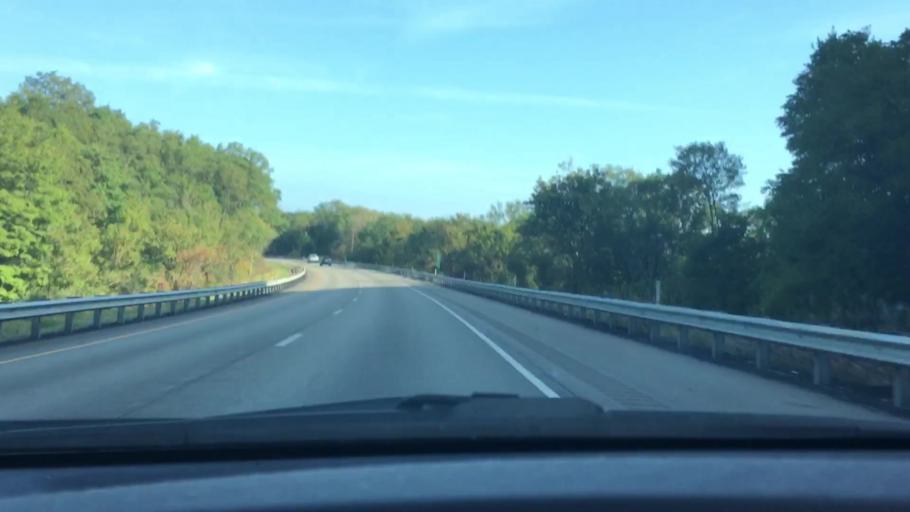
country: US
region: Pennsylvania
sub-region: Butler County
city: Evans City
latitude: 40.7493
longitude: -80.1065
